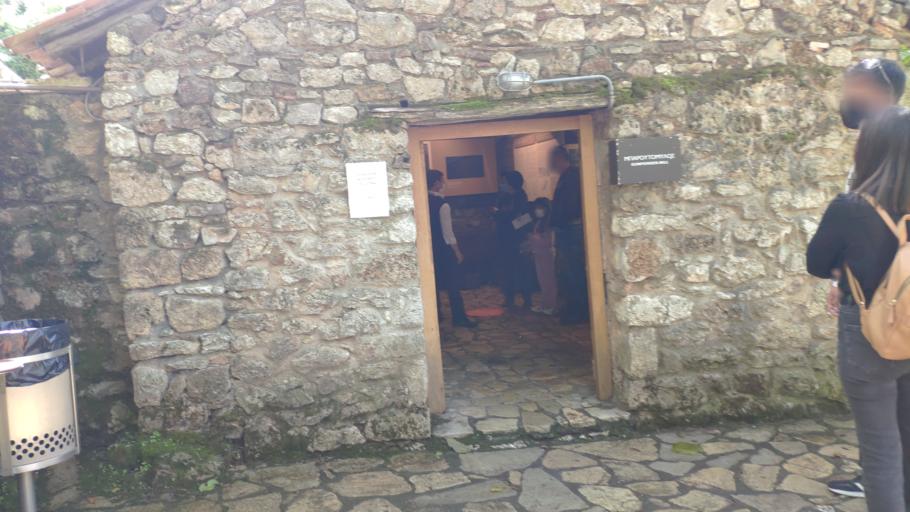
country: GR
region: Peloponnese
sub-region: Nomos Arkadias
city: Dimitsana
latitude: 37.5831
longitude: 22.0469
